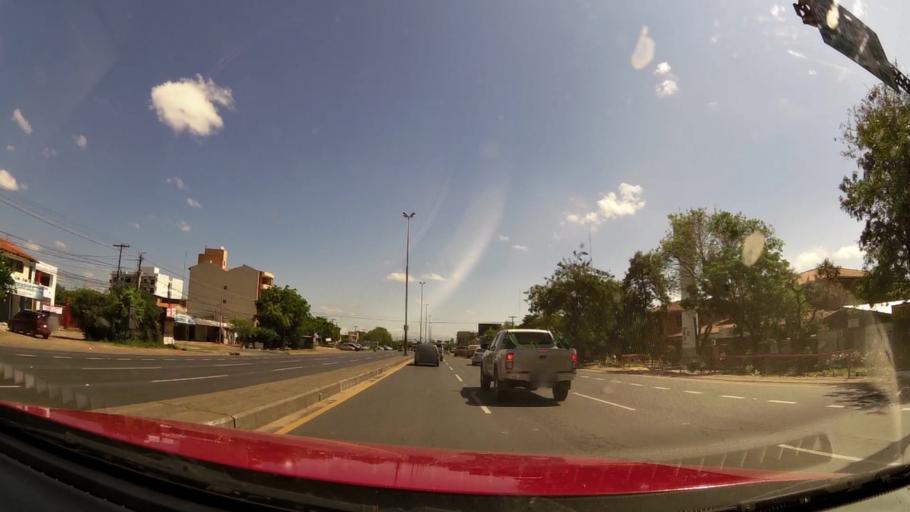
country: PY
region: Central
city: Colonia Mariano Roque Alonso
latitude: -25.2415
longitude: -57.5441
